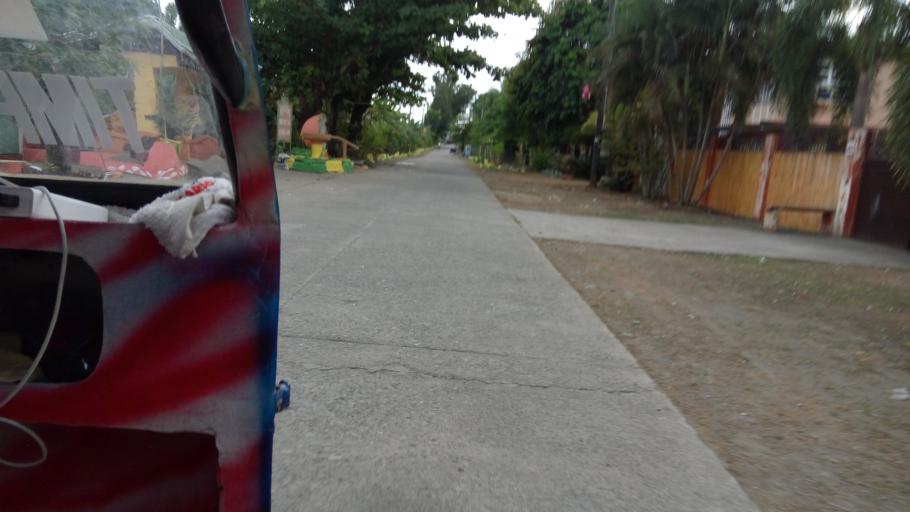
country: PH
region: Ilocos
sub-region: Province of La Union
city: Santo Tomas
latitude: 16.2862
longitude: 120.3821
